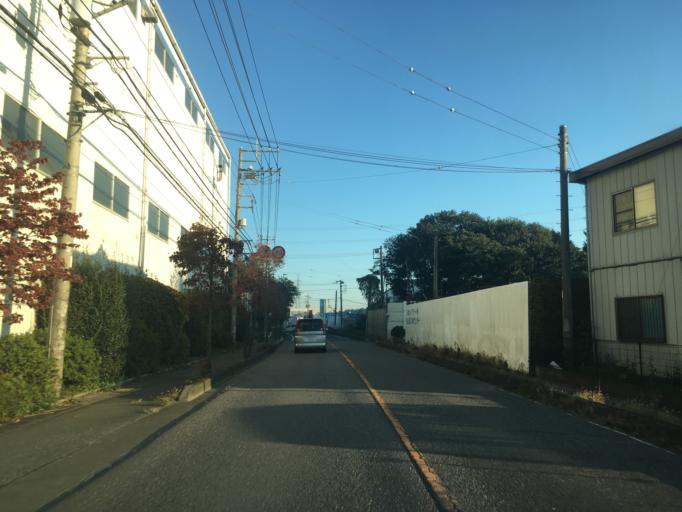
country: JP
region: Saitama
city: Tokorozawa
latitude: 35.8388
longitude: 139.4662
